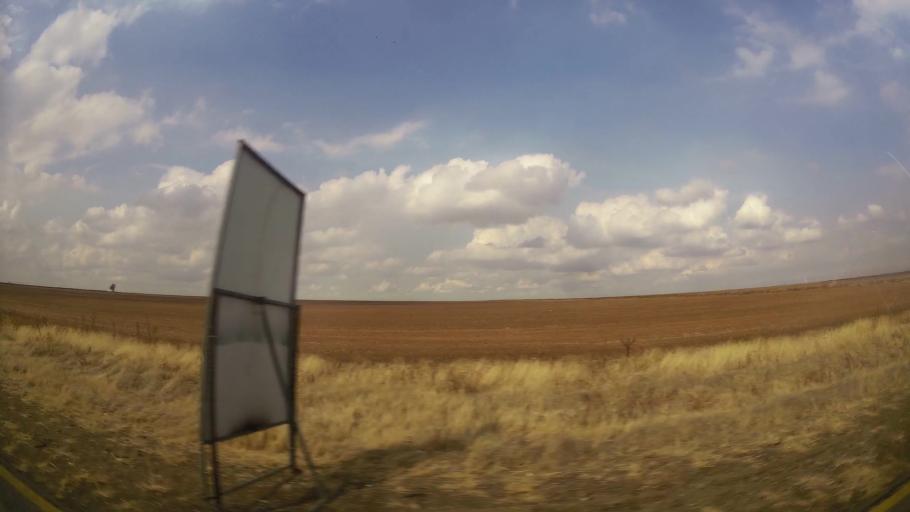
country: ZA
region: Orange Free State
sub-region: Fezile Dabi District Municipality
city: Sasolburg
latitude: -26.8377
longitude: 27.8948
